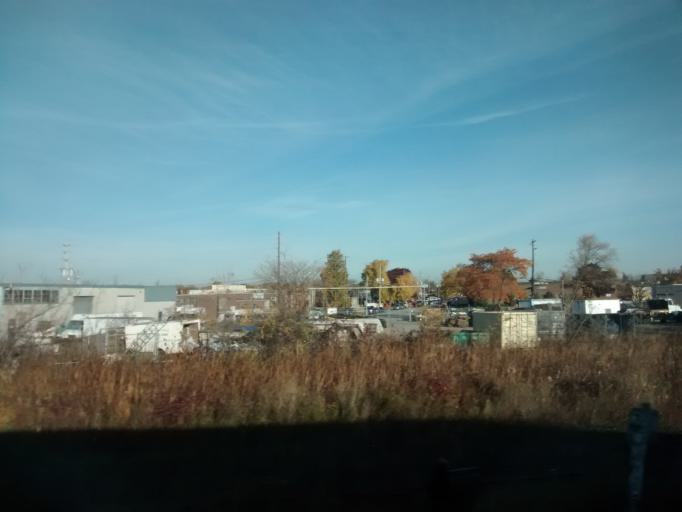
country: CA
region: Ontario
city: Etobicoke
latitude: 43.6014
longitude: -79.5265
